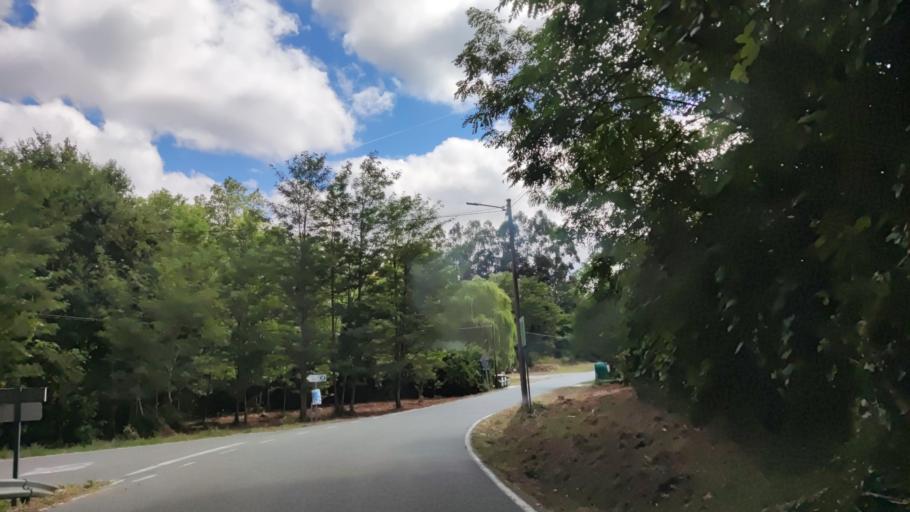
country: ES
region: Galicia
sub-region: Provincia da Coruna
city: Rois
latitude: 42.7824
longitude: -8.6683
